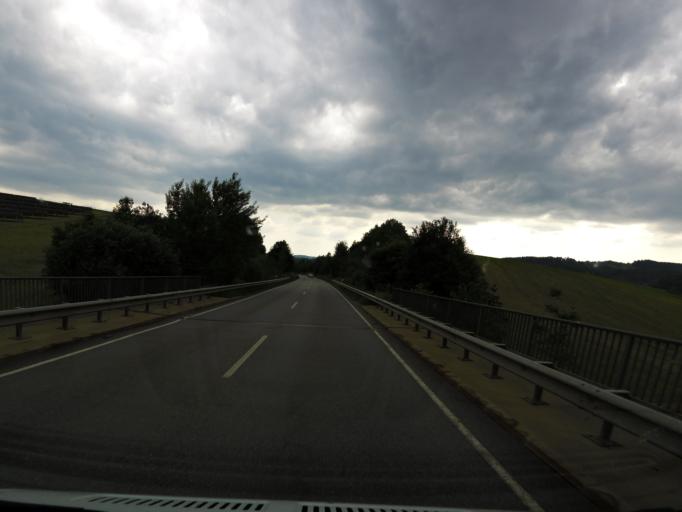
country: DE
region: Bavaria
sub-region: Lower Bavaria
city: Neukirchen vorm Wald
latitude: 48.6902
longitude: 13.3731
